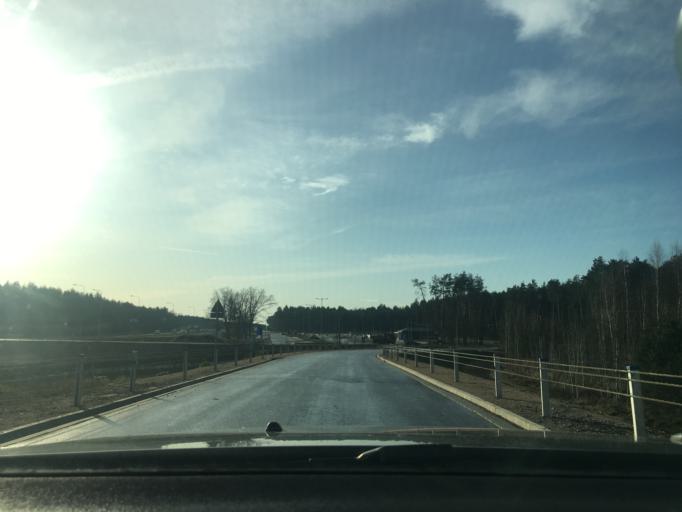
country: PL
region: Swietokrzyskie
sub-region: Powiat jedrzejowski
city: Jedrzejow
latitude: 50.6854
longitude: 20.3564
